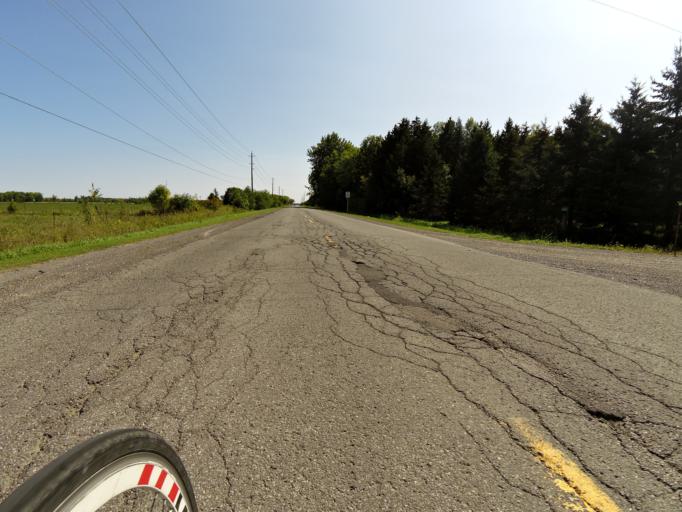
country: CA
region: Ontario
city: Arnprior
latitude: 45.4773
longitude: -76.1185
